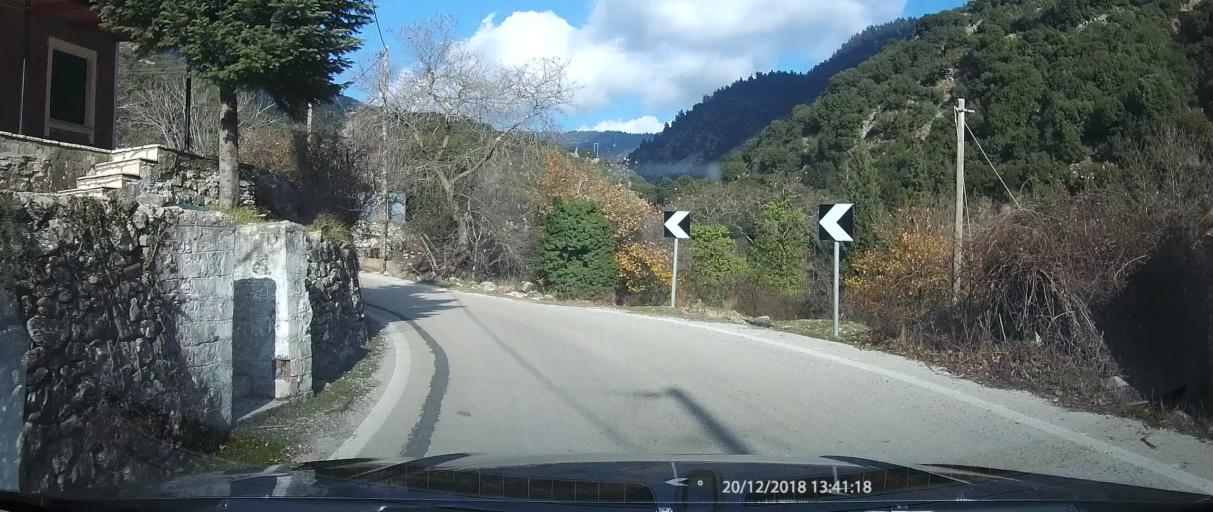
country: GR
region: West Greece
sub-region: Nomos Aitolias kai Akarnanias
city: Thermo
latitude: 38.6478
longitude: 21.6147
